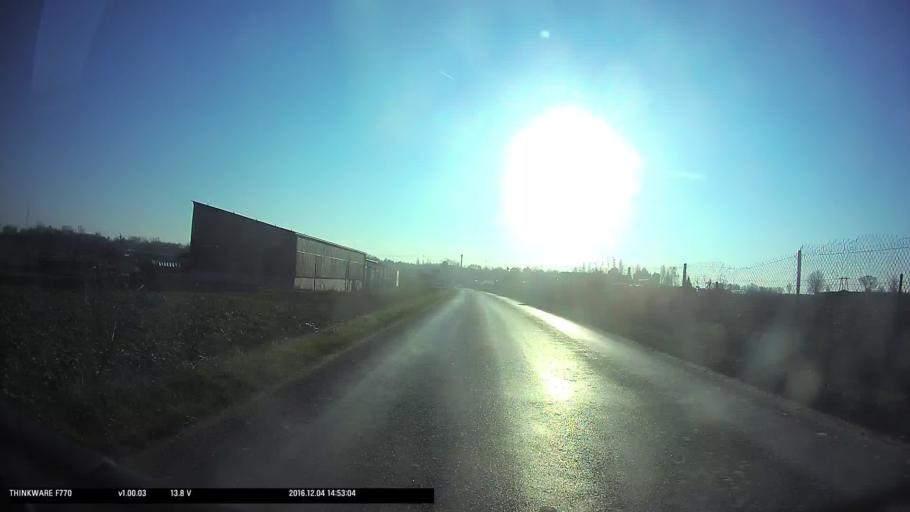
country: FR
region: Ile-de-France
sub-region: Departement du Val-d'Oise
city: Courdimanche
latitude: 49.0632
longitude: 2.0022
